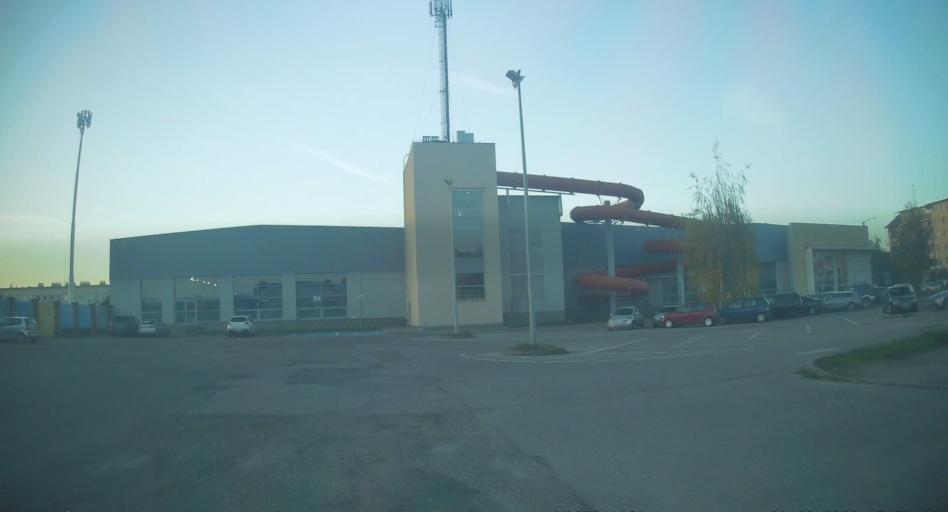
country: PL
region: Subcarpathian Voivodeship
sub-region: Powiat debicki
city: Debica
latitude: 50.0583
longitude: 21.4001
